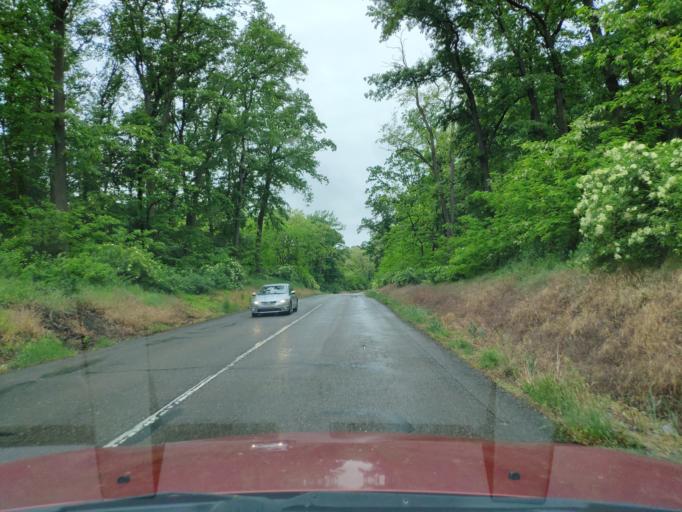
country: HU
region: Borsod-Abauj-Zemplen
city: Ricse
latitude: 48.4360
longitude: 21.9507
